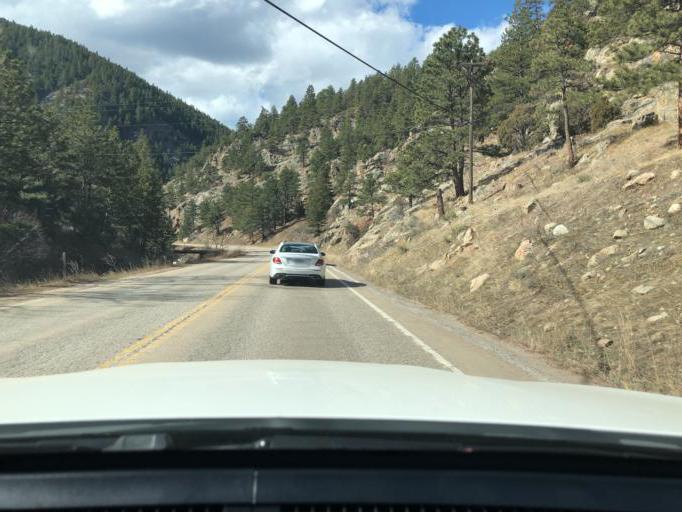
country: US
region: Colorado
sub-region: Boulder County
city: Coal Creek
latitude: 40.0033
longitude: -105.3677
